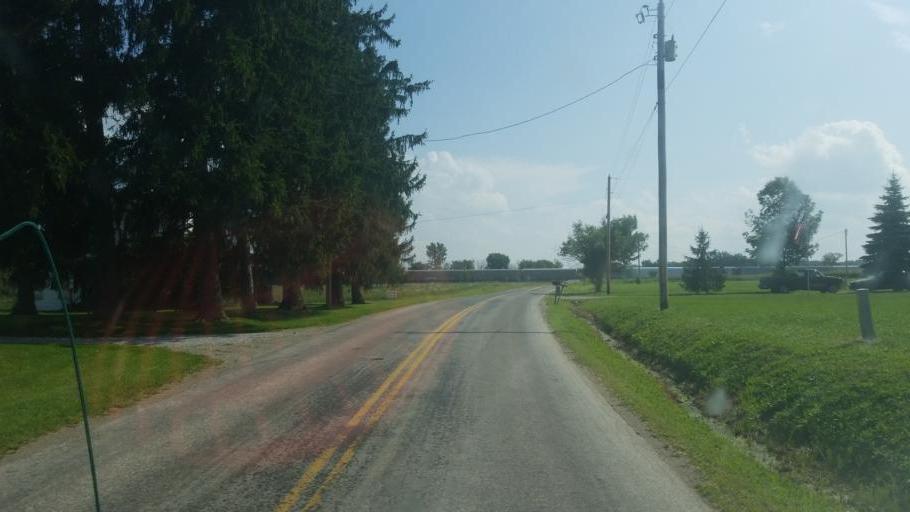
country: US
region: Ohio
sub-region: Wayne County
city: West Salem
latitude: 41.0489
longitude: -82.1818
